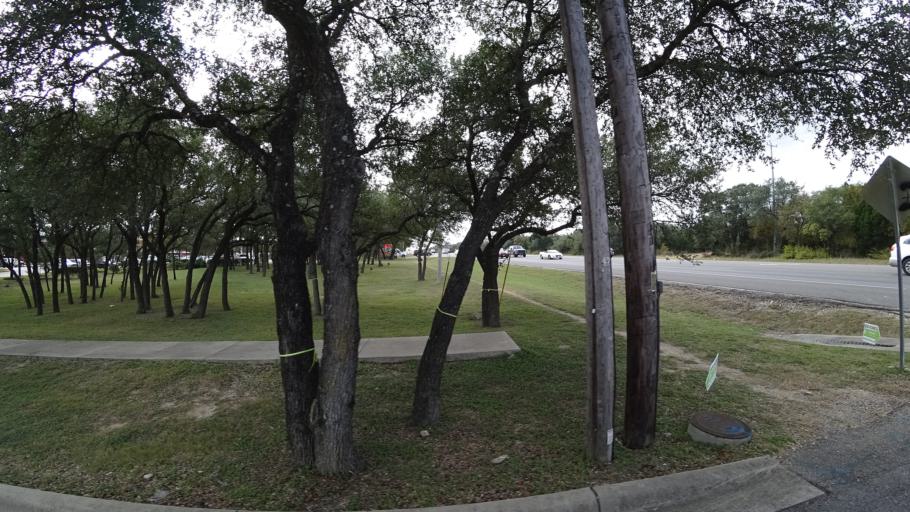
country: US
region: Texas
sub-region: Williamson County
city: Anderson Mill
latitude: 30.4117
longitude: -97.8497
